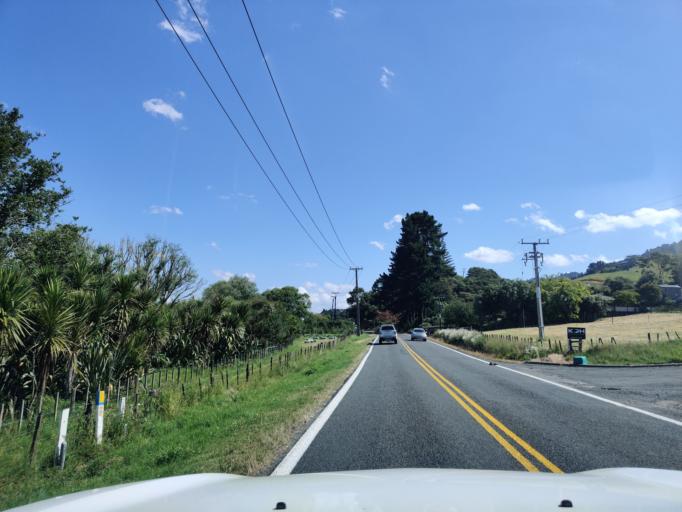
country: NZ
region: Waikato
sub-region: Waikato District
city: Ngaruawahia
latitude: -37.6504
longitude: 175.1449
